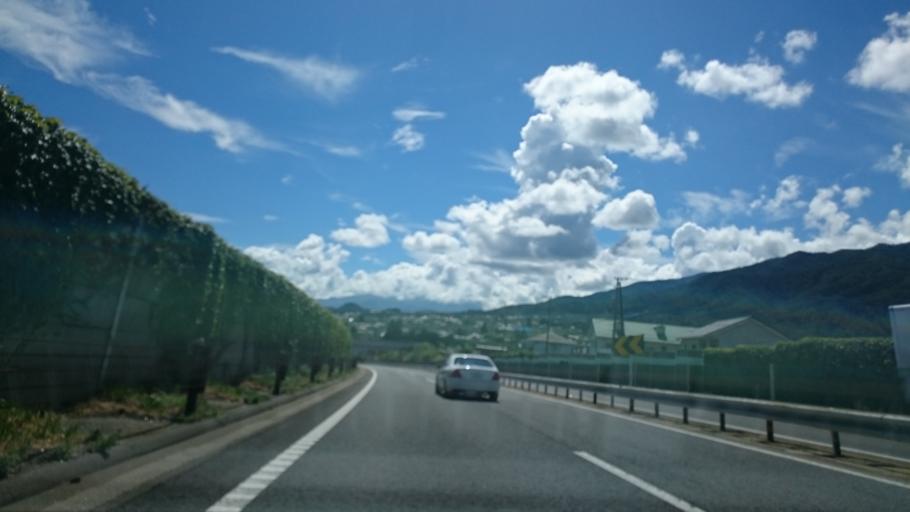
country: JP
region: Nagano
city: Iida
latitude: 35.5192
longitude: 137.8060
